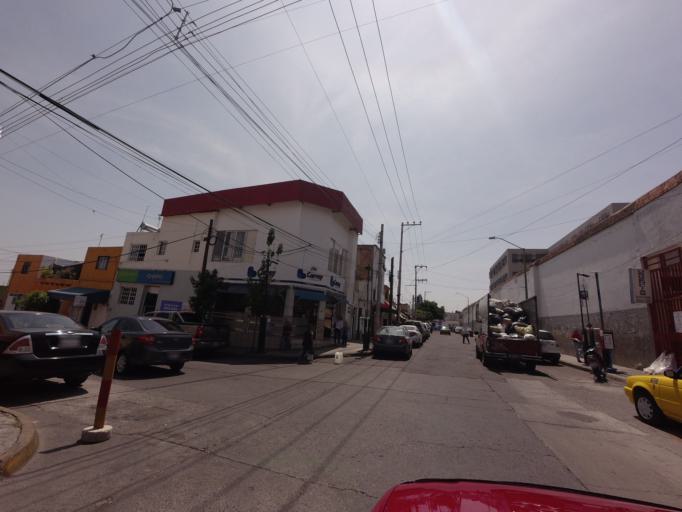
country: MX
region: Jalisco
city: Guadalajara
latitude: 20.6889
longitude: -103.3439
